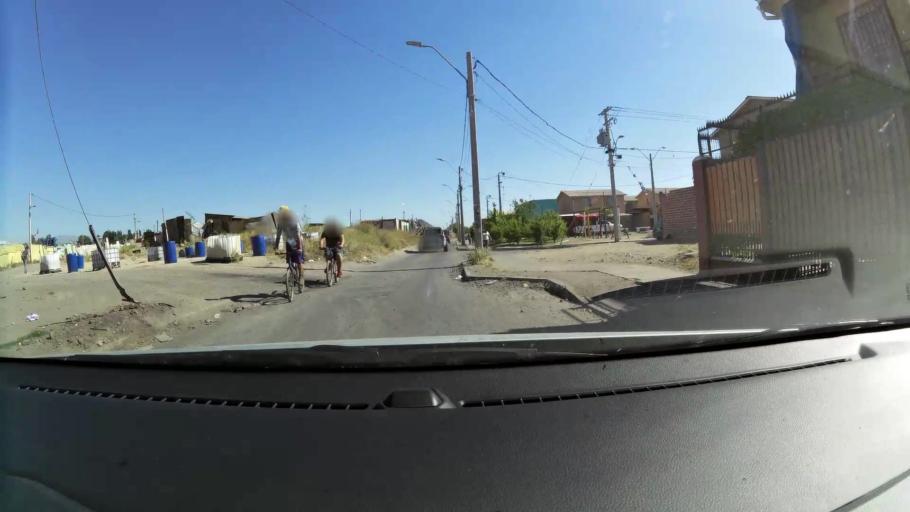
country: CL
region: Santiago Metropolitan
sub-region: Provincia de Maipo
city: San Bernardo
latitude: -33.5915
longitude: -70.6675
